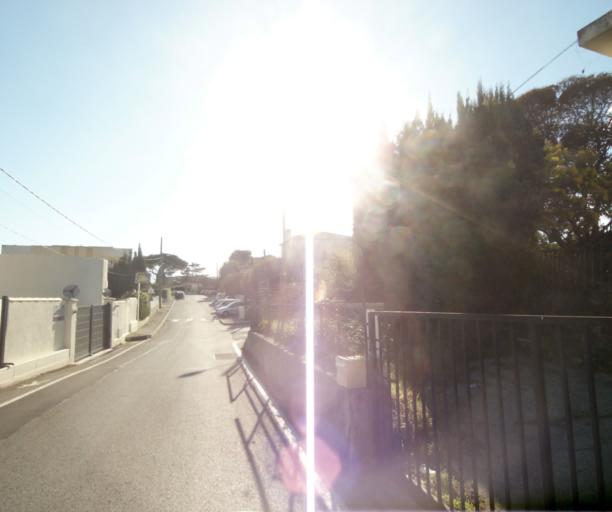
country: FR
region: Provence-Alpes-Cote d'Azur
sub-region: Departement des Alpes-Maritimes
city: Biot
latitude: 43.6074
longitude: 7.1215
